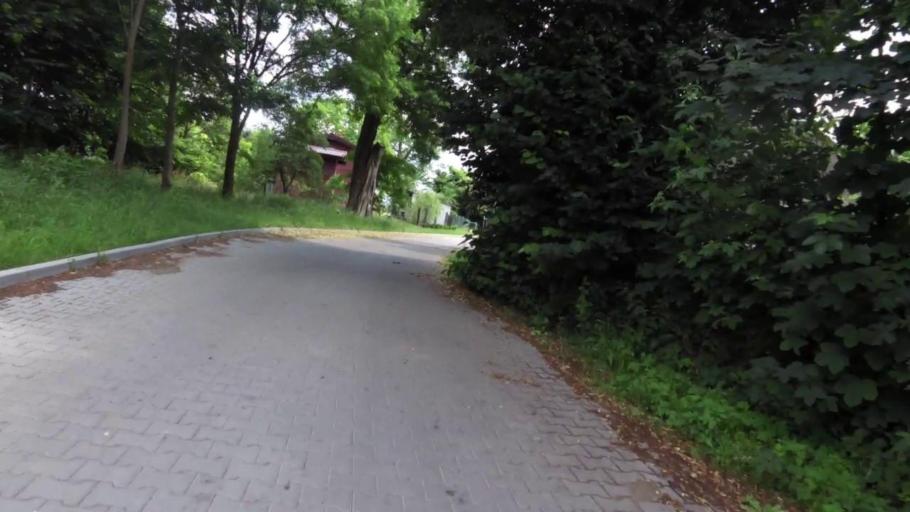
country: PL
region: West Pomeranian Voivodeship
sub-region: Powiat mysliborski
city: Nowogrodek Pomorski
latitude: 52.9874
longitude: 15.0630
